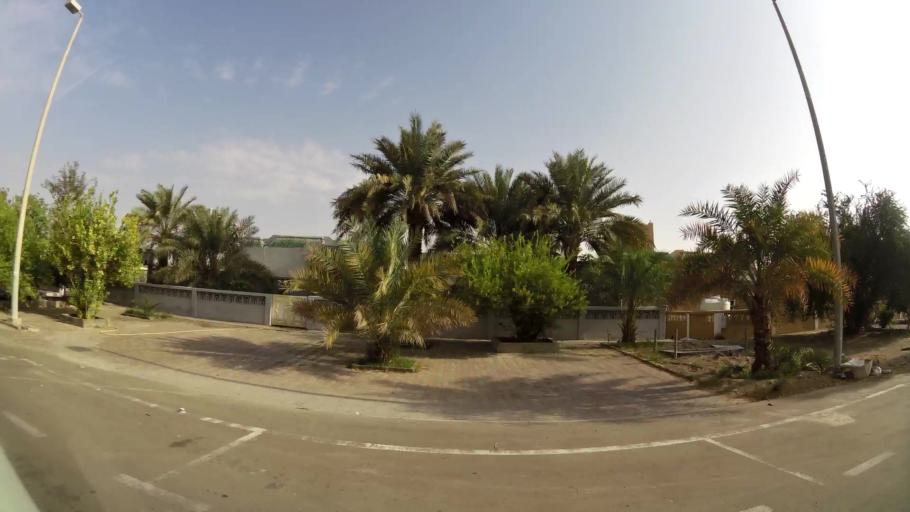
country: AE
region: Abu Dhabi
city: Abu Dhabi
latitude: 24.2608
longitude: 54.6690
